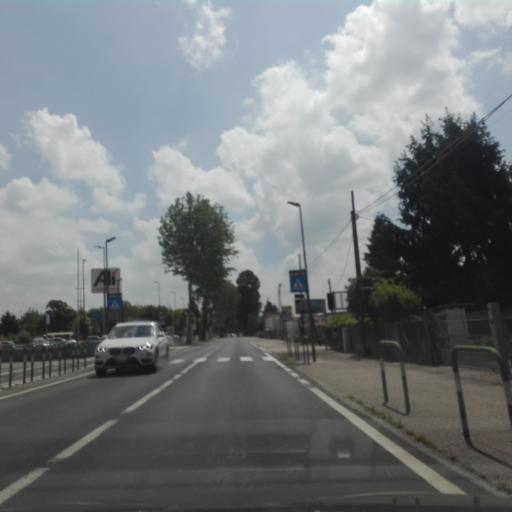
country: IT
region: Veneto
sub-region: Provincia di Rovigo
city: Villadose
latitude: 45.0692
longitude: 11.8884
